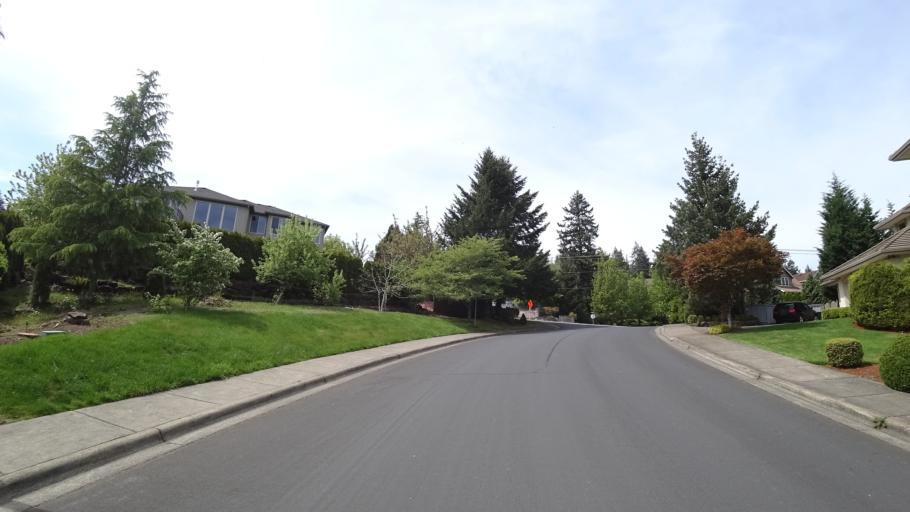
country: US
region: Oregon
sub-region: Washington County
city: Aloha
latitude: 45.4550
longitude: -122.8563
